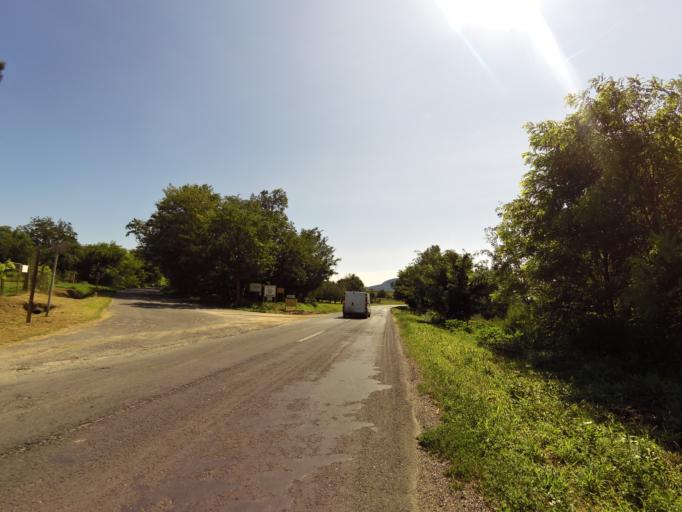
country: HU
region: Veszprem
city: Tapolca
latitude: 46.8307
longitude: 17.4390
